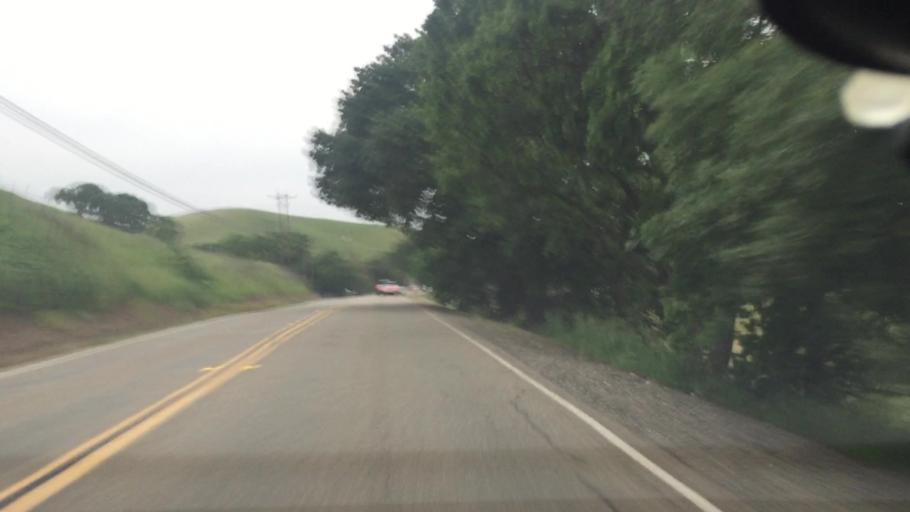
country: US
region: California
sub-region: Alameda County
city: Livermore
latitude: 37.6505
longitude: -121.6594
